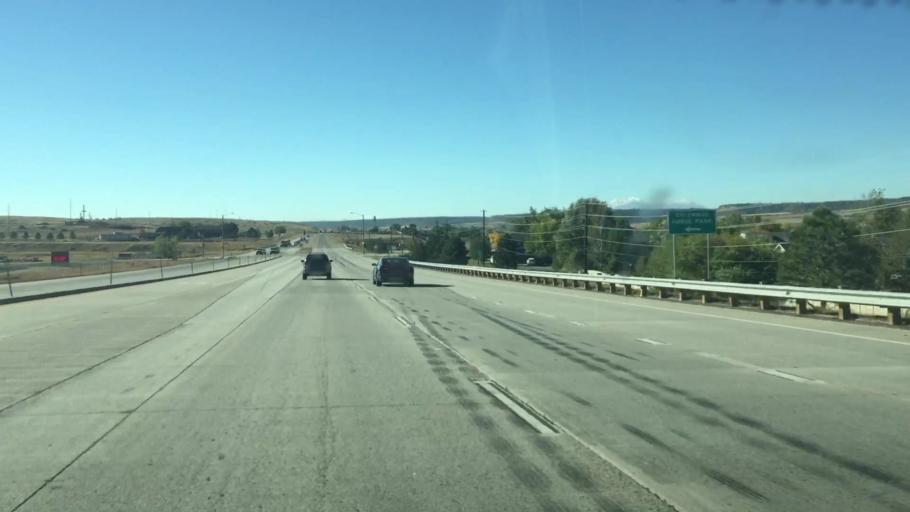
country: US
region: Colorado
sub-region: Douglas County
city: The Pinery
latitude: 39.4372
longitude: -104.7604
